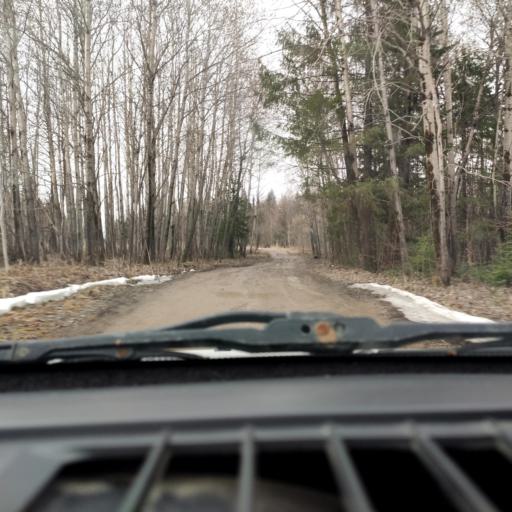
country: RU
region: Perm
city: Kultayevo
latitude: 57.8221
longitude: 55.7970
